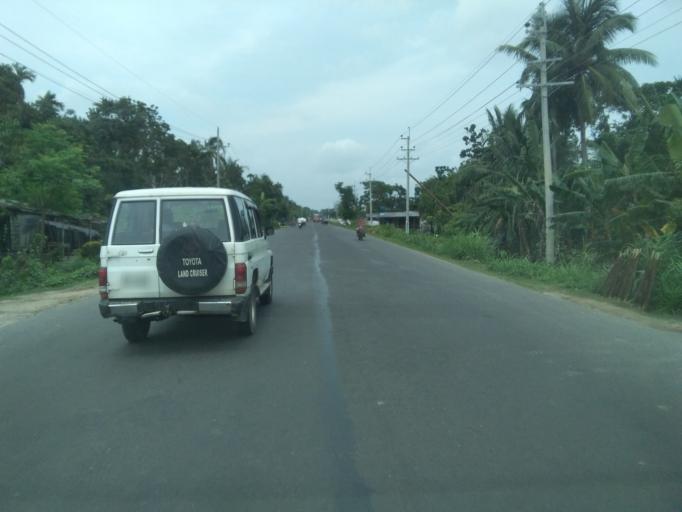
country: BD
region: Khulna
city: Satkhira
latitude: 22.7677
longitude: 89.1498
